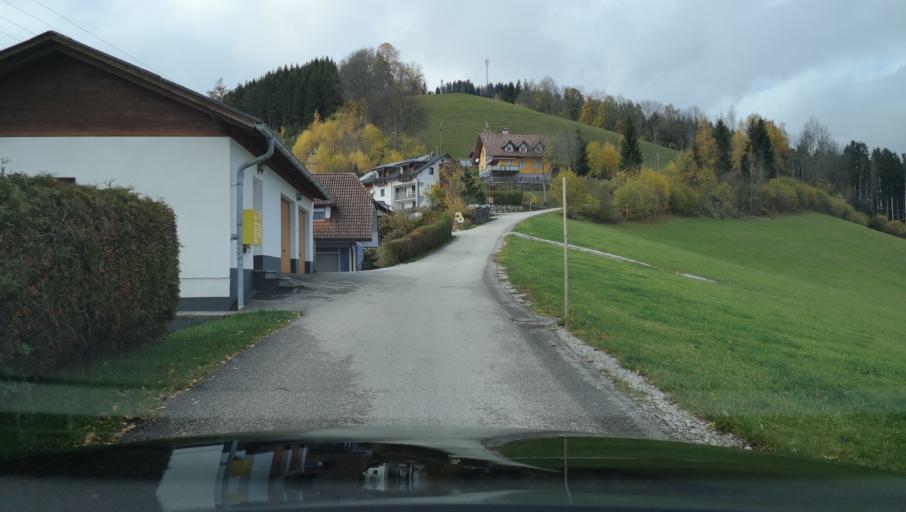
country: AT
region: Styria
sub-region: Politischer Bezirk Weiz
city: Birkfeld
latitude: 47.3645
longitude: 15.6504
